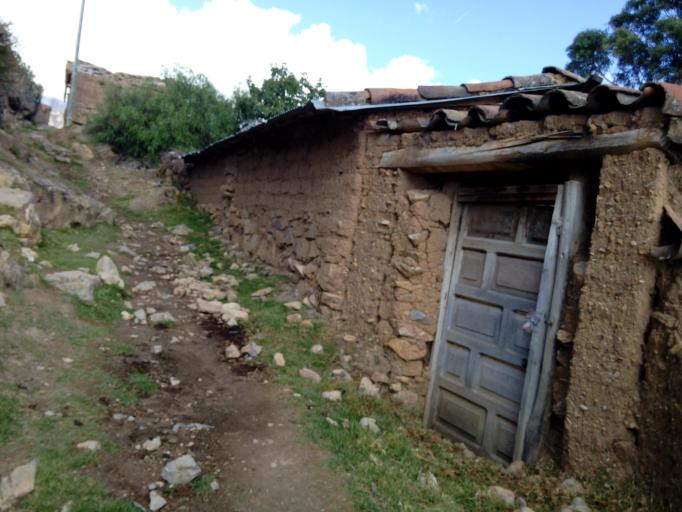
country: PE
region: Ayacucho
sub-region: Provincia de Victor Fajardo
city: Canaria
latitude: -13.8797
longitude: -73.9313
